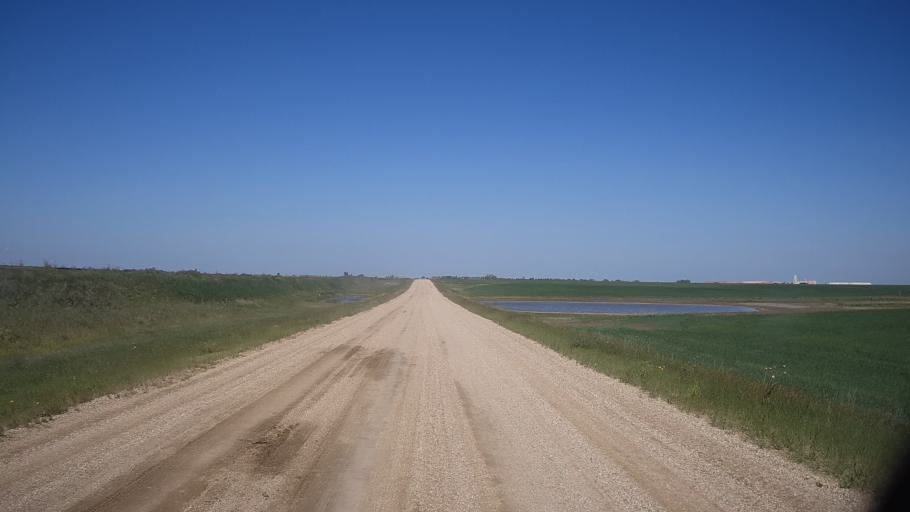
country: CA
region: Saskatchewan
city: Watrous
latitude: 51.8772
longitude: -106.0119
